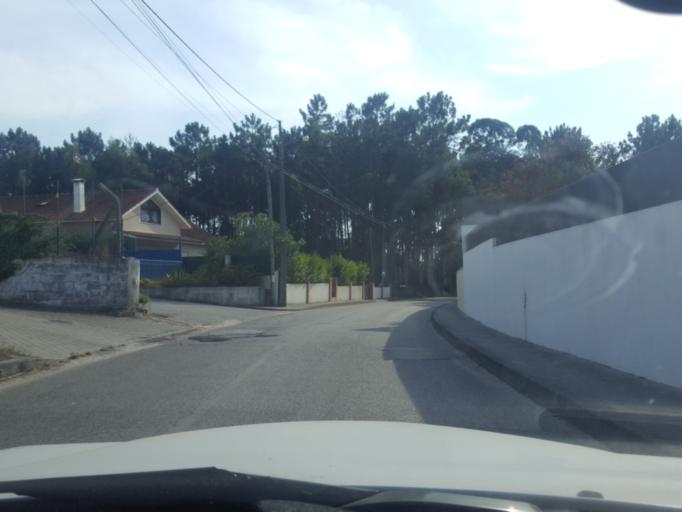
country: PT
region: Leiria
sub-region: Leiria
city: Leiria
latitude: 39.7292
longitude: -8.7638
